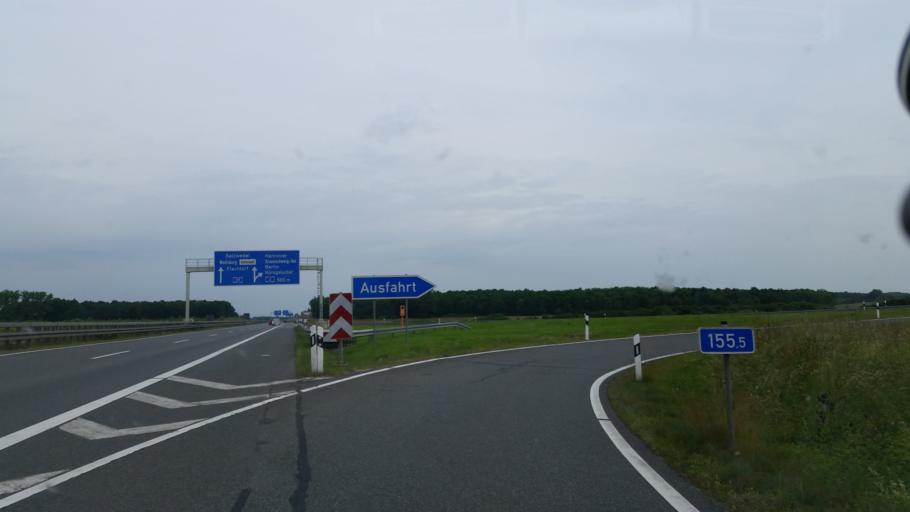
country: DE
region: Lower Saxony
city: Lehre
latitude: 52.2972
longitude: 10.7212
